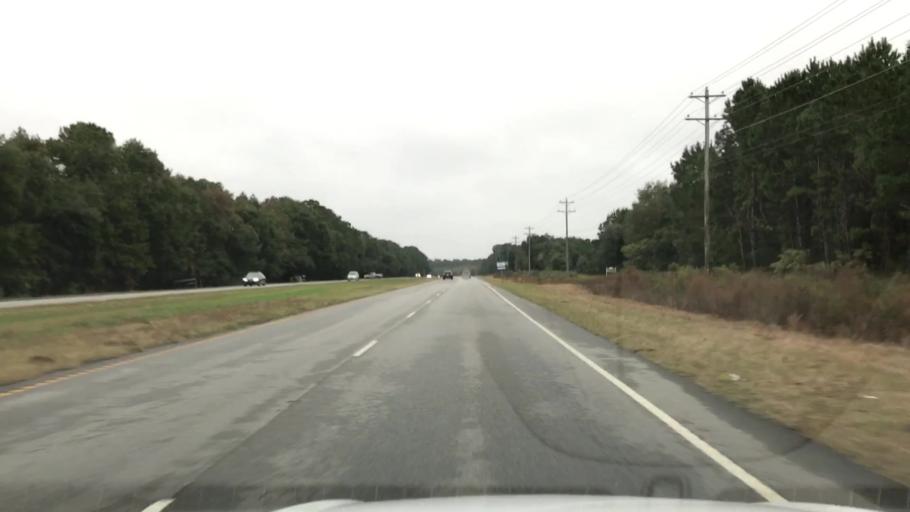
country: US
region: South Carolina
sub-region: Charleston County
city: Isle of Palms
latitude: 32.9123
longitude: -79.7213
